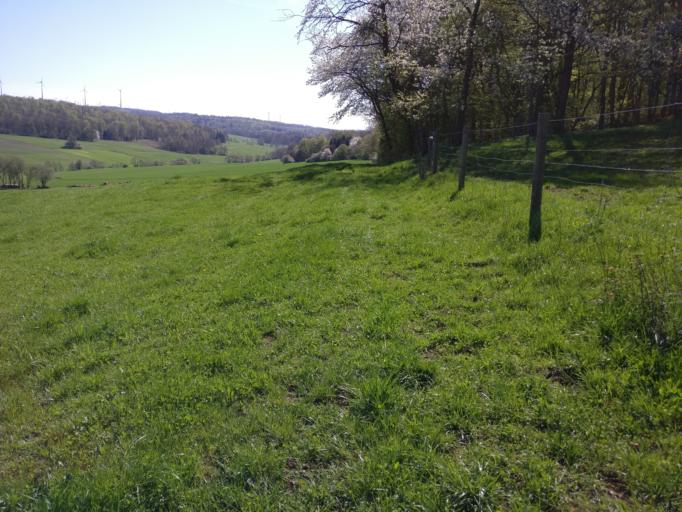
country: DE
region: Hesse
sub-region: Regierungsbezirk Giessen
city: Schwalmtal
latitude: 50.6508
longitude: 9.2447
